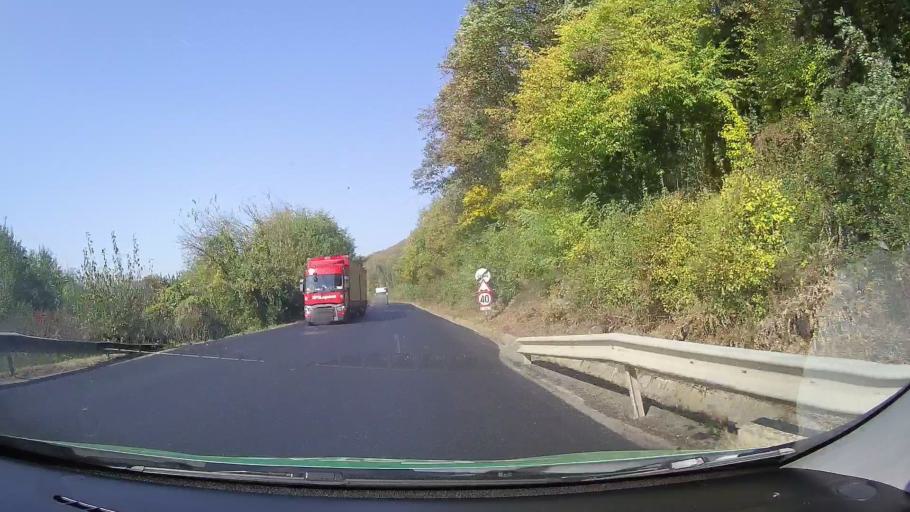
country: RO
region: Hunedoara
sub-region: Comuna Zam
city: Zam
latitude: 46.0137
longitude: 22.4262
